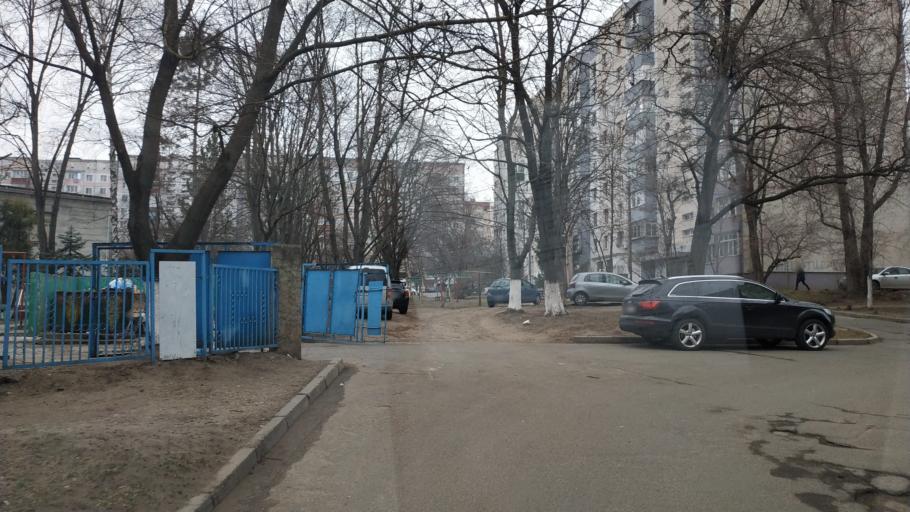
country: MD
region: Chisinau
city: Vatra
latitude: 47.0380
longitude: 28.7755
